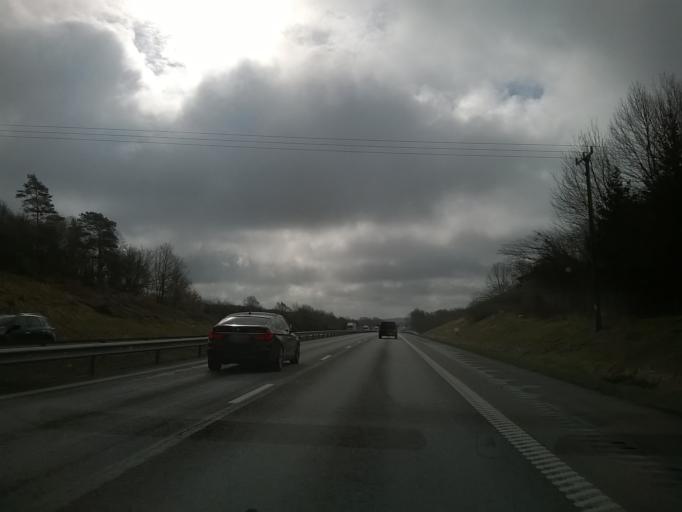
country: SE
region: Halland
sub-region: Varbergs Kommun
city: Varberg
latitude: 57.1455
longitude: 12.2998
